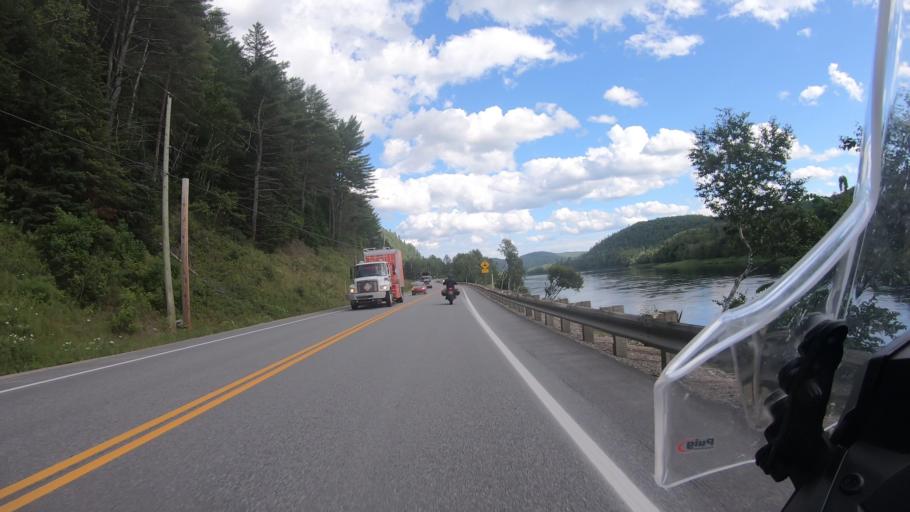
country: CA
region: Quebec
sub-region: Mauricie
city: Saint-Tite
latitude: 46.9944
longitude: -72.9171
